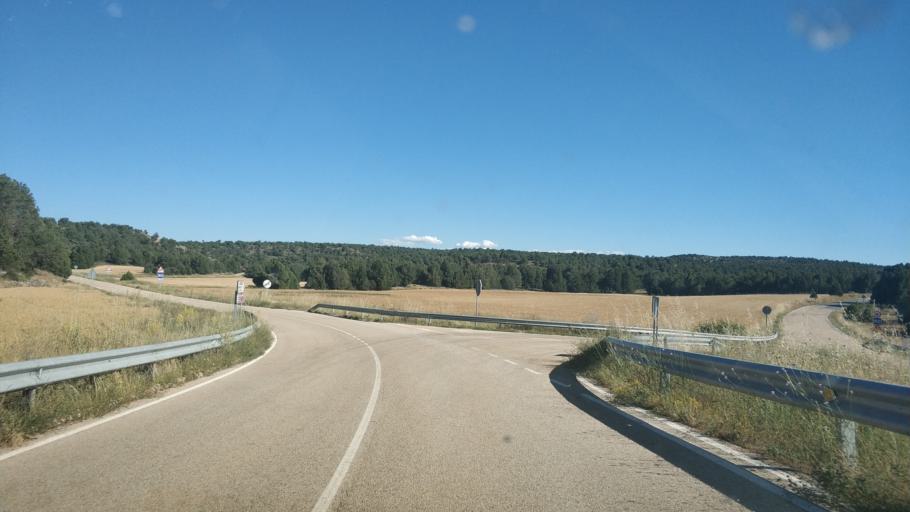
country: ES
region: Castille and Leon
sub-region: Provincia de Soria
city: Liceras
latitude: 41.4390
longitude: -3.2143
